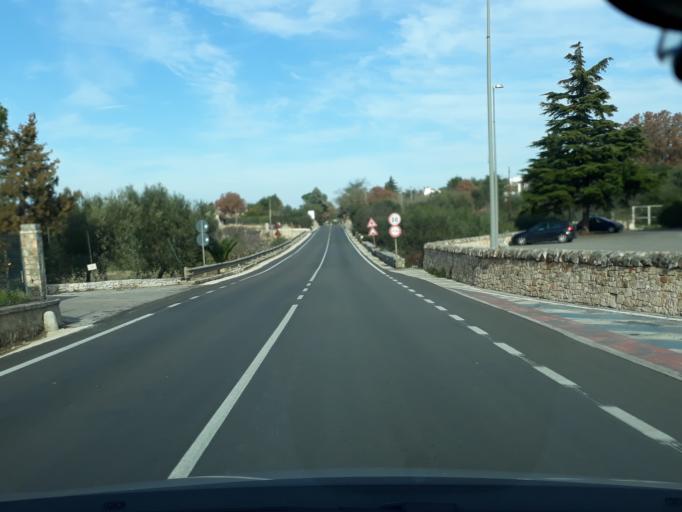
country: IT
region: Apulia
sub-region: Provincia di Bari
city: Locorotondo
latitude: 40.7761
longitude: 17.3362
